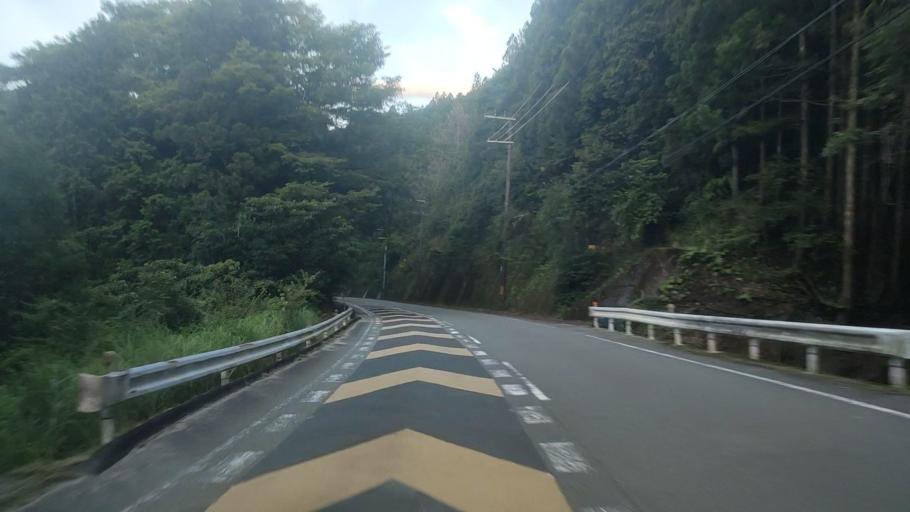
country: JP
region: Wakayama
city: Shingu
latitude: 33.8068
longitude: 135.7271
